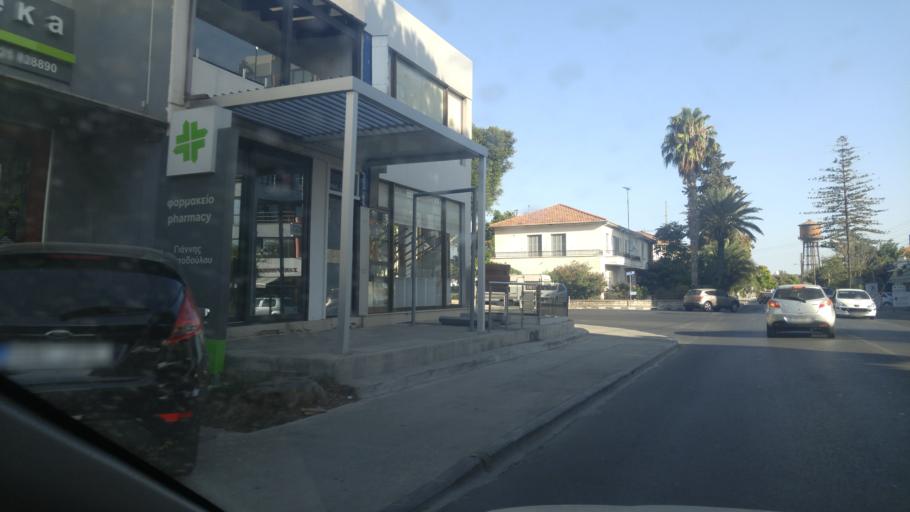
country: CY
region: Limassol
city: Limassol
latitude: 34.6805
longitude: 33.0350
